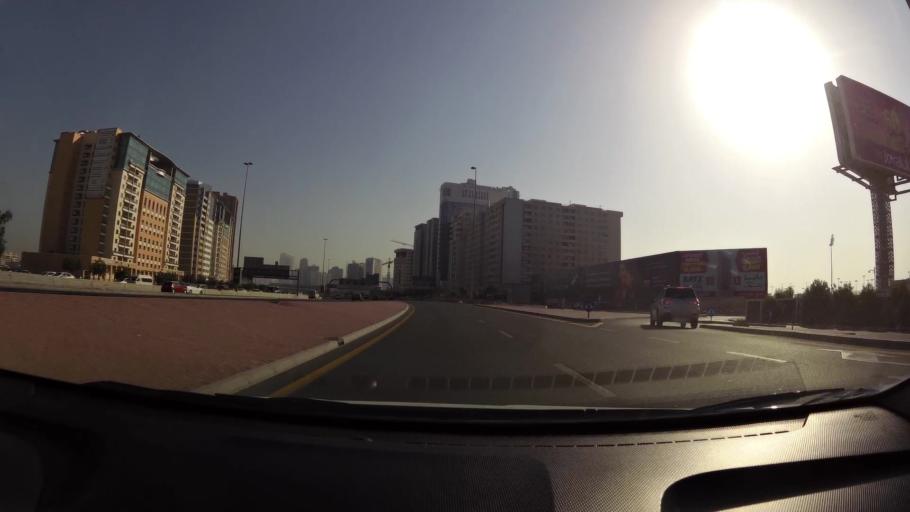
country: AE
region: Ash Shariqah
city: Sharjah
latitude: 25.2829
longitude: 55.3581
